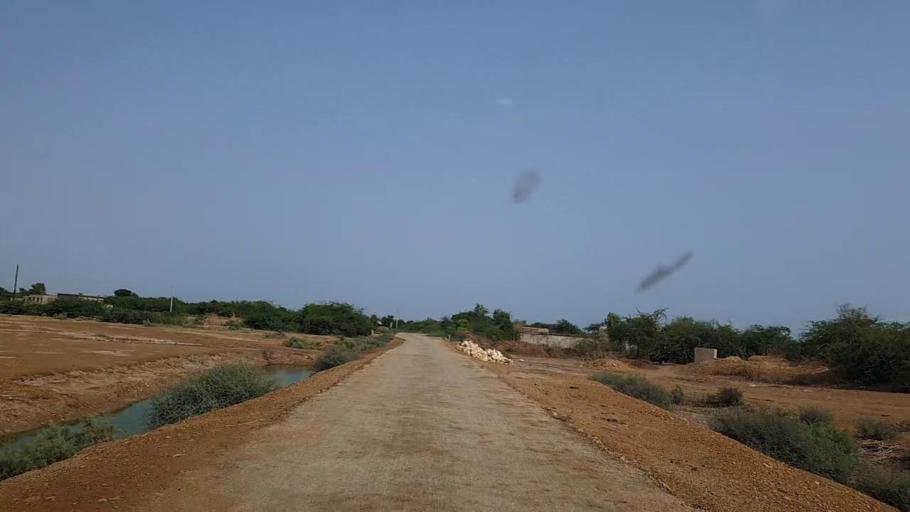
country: PK
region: Sindh
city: Kotri
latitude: 25.2461
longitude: 68.2401
